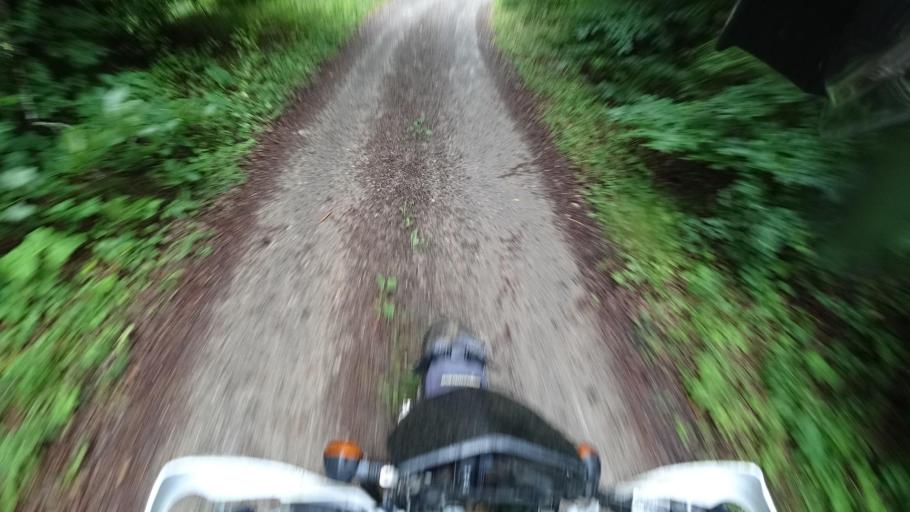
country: HR
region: Karlovacka
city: Plaski
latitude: 44.9043
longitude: 15.4136
